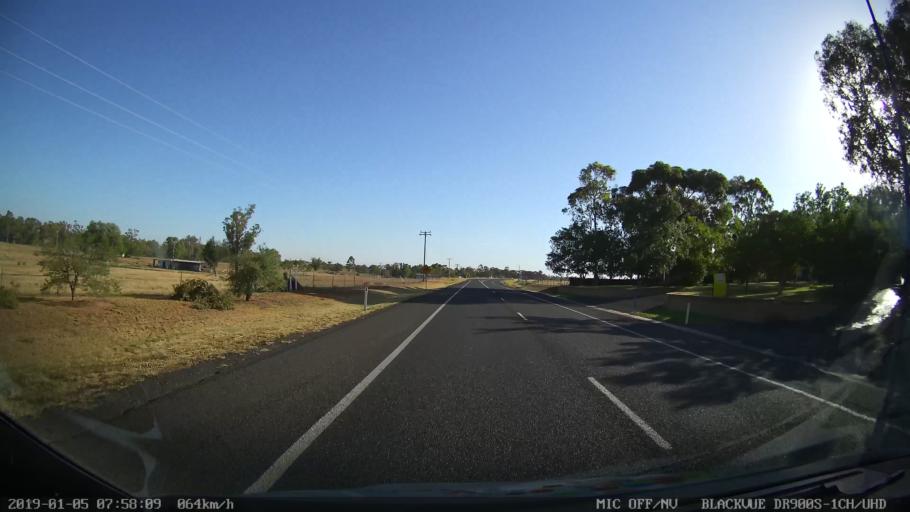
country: AU
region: New South Wales
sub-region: Gilgandra
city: Gilgandra
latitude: -31.7143
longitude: 148.6735
